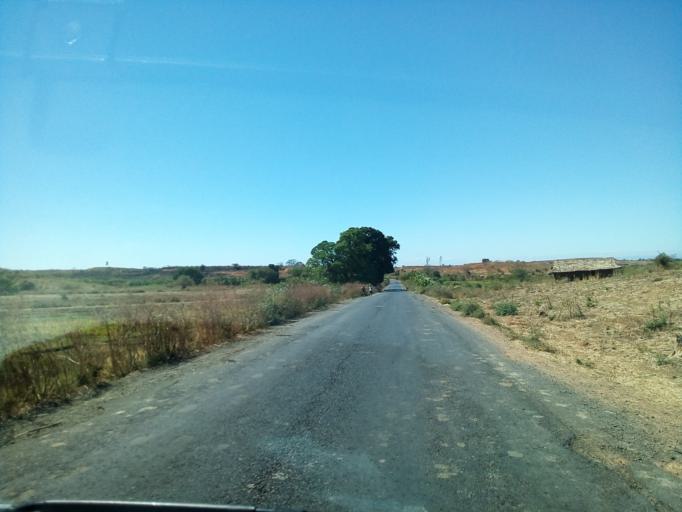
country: MG
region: Boeny
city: Ambato Boeny
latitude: -16.3807
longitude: 46.9285
